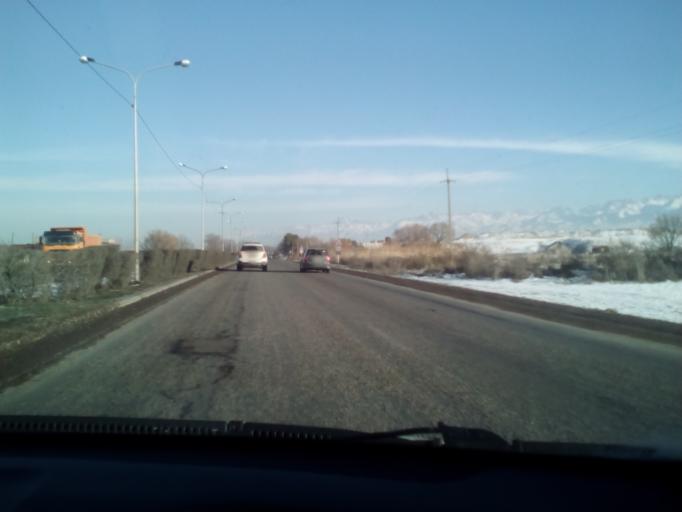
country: KZ
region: Almaty Oblysy
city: Burunday
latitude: 43.2225
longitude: 76.4220
